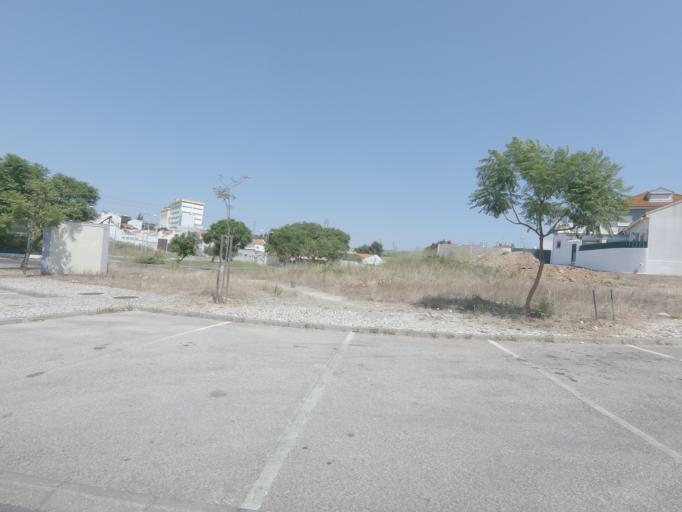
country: PT
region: Setubal
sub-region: Setubal
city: Setubal
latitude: 38.5432
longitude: -8.8839
